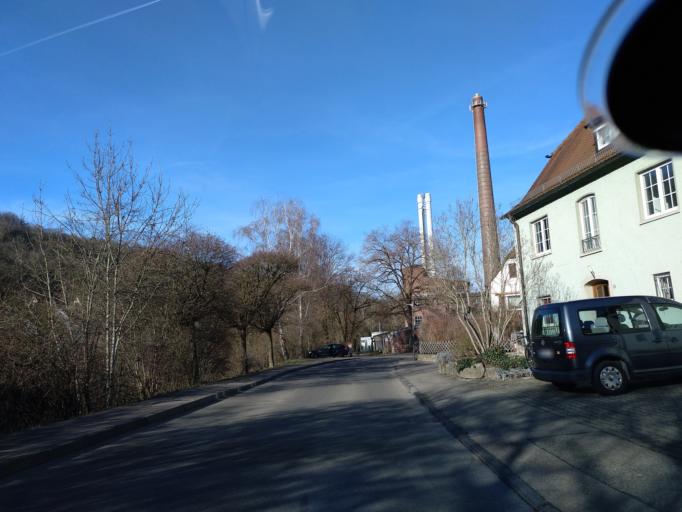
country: DE
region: Baden-Wuerttemberg
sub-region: Regierungsbezirk Stuttgart
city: Schwaebisch Hall
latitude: 49.1198
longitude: 9.7327
